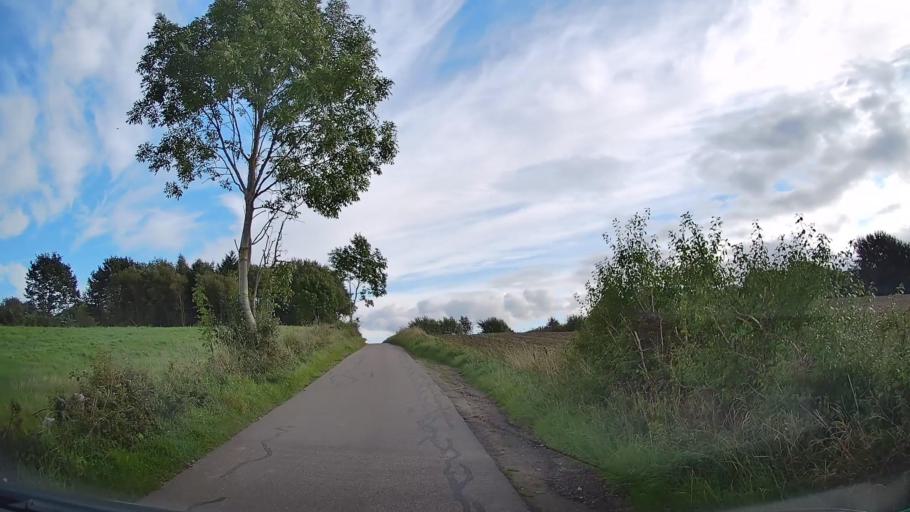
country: DE
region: Schleswig-Holstein
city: Ringsberg
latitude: 54.8279
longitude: 9.6041
